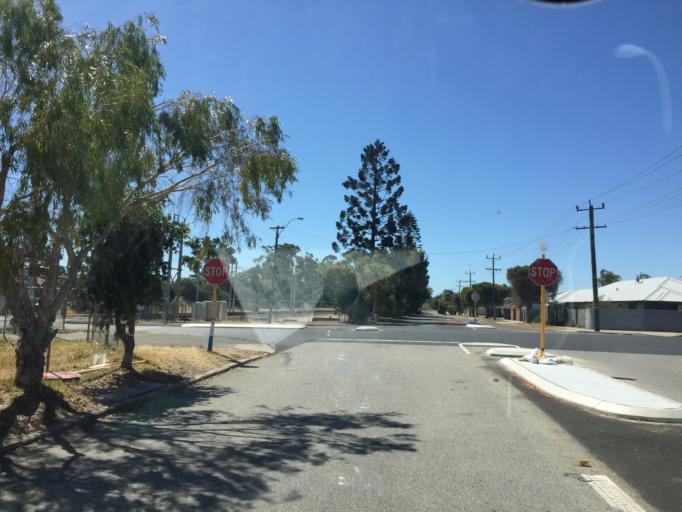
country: AU
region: Western Australia
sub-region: Victoria Park
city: Victoria Park
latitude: -31.9795
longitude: 115.9101
